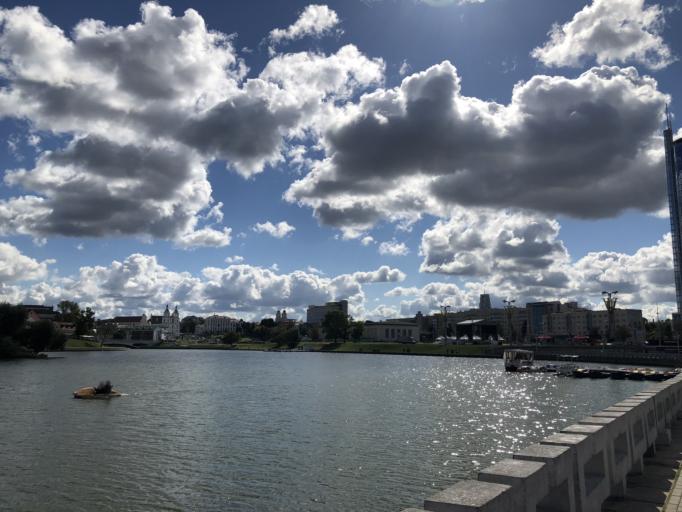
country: BY
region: Minsk
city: Minsk
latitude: 53.9104
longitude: 27.5524
